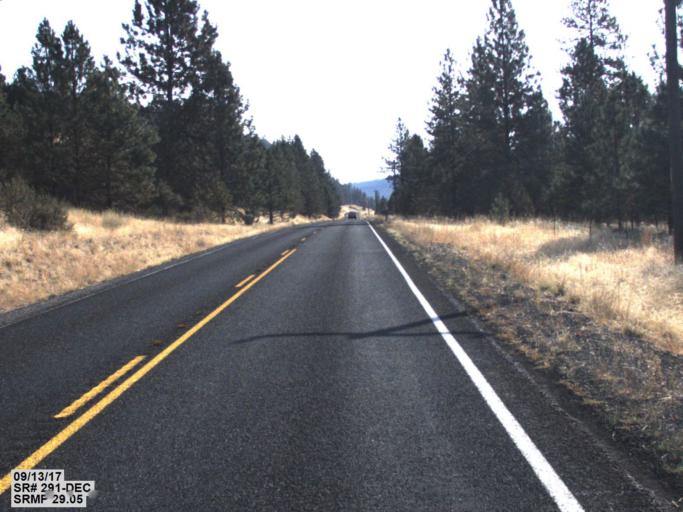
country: US
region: Washington
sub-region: Spokane County
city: Fairchild Air Force Base
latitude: 47.8391
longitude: -117.7750
